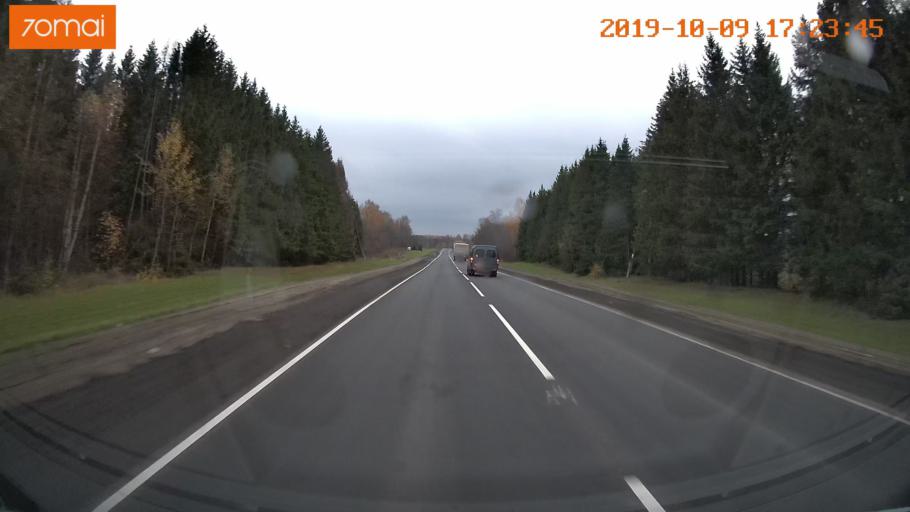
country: RU
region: Ivanovo
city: Furmanov
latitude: 57.1921
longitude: 41.1140
